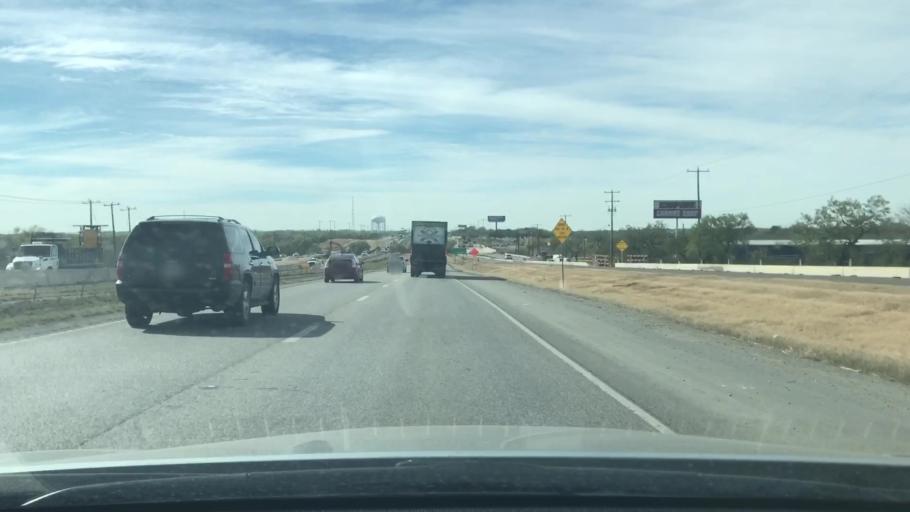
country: US
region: Texas
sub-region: Bexar County
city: Converse
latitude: 29.4571
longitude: -98.3242
